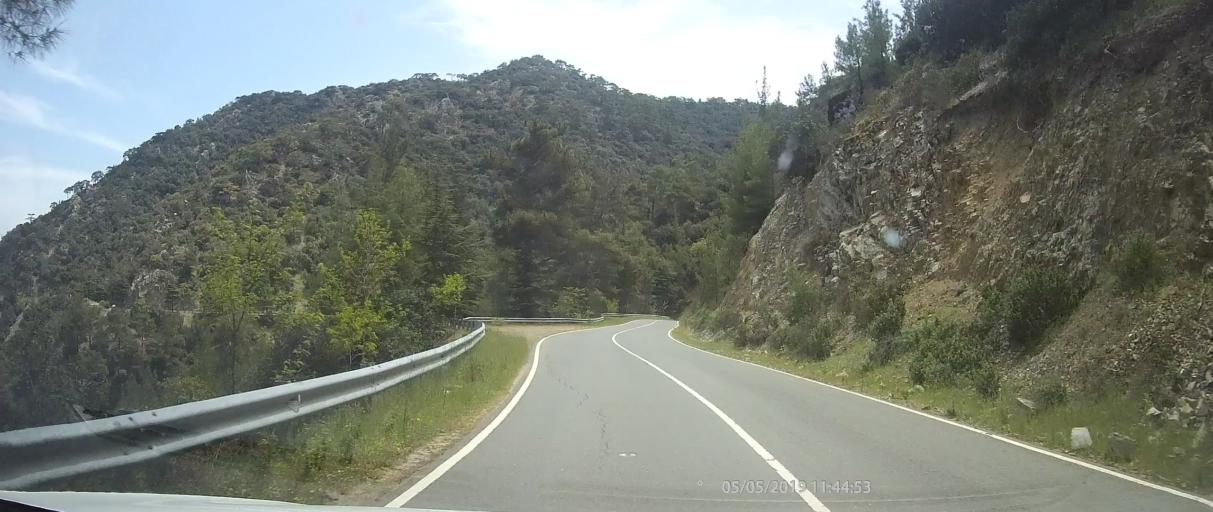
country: CY
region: Lefkosia
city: Kato Pyrgos
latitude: 35.0119
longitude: 32.6723
